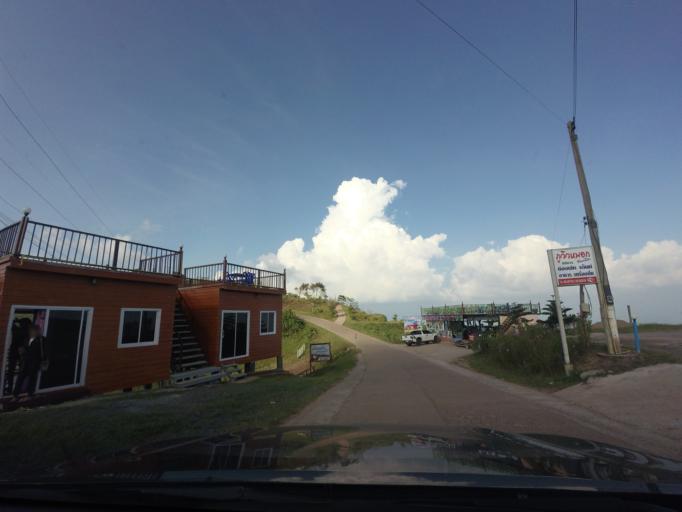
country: TH
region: Phetchabun
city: Lom Kao
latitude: 16.9038
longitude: 101.1091
